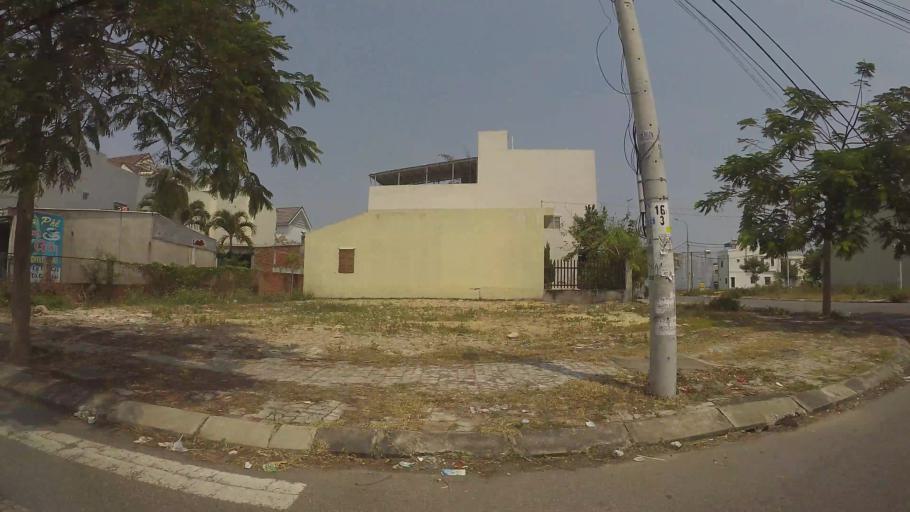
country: VN
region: Da Nang
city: Ngu Hanh Son
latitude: 15.9929
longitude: 108.2660
